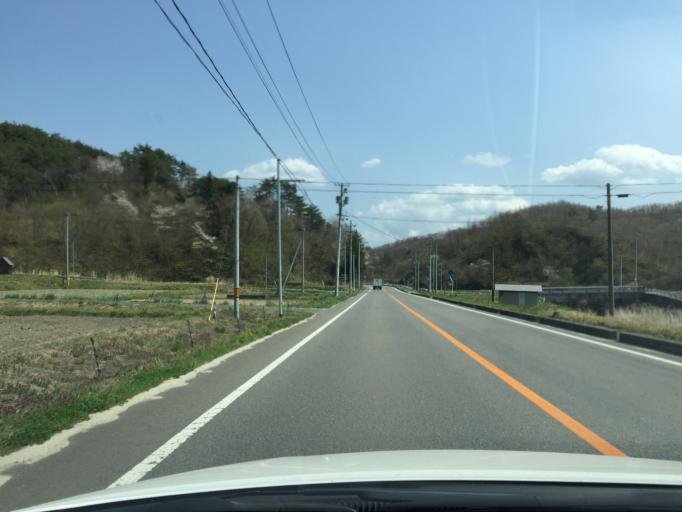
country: JP
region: Fukushima
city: Funehikimachi-funehiki
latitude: 37.4497
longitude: 140.7706
